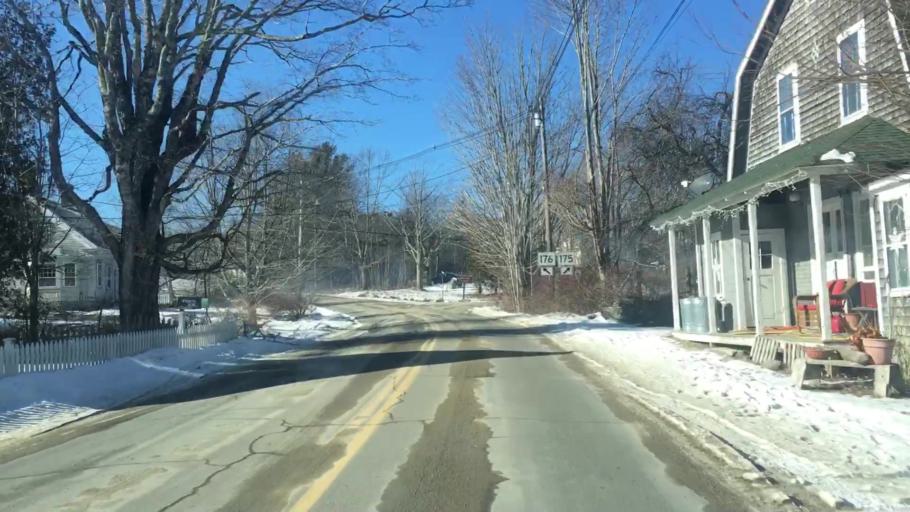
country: US
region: Maine
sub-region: Hancock County
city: Sedgwick
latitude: 44.3466
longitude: -68.6834
